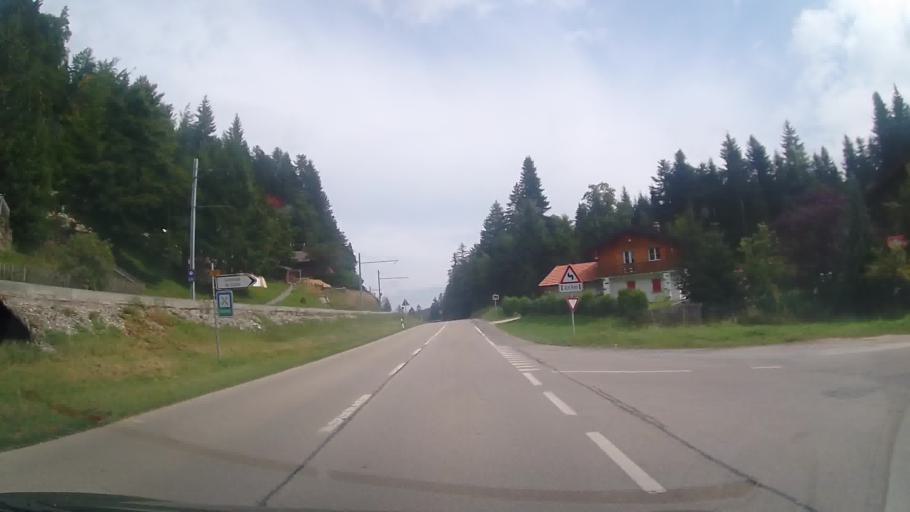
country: CH
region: Vaud
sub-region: Nyon District
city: Saint-Cergue
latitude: 46.4509
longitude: 6.1272
